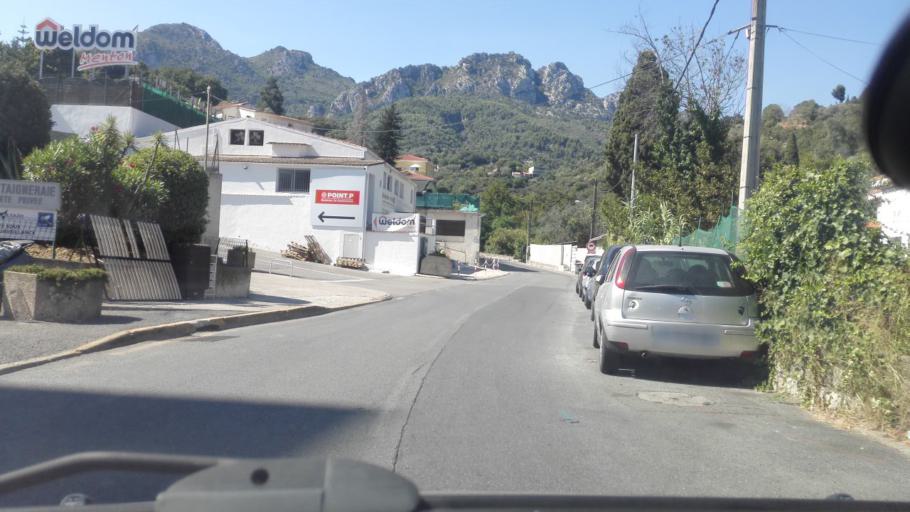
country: FR
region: Provence-Alpes-Cote d'Azur
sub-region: Departement des Alpes-Maritimes
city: Roquebrune-Cap-Martin
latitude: 43.7820
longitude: 7.4799
